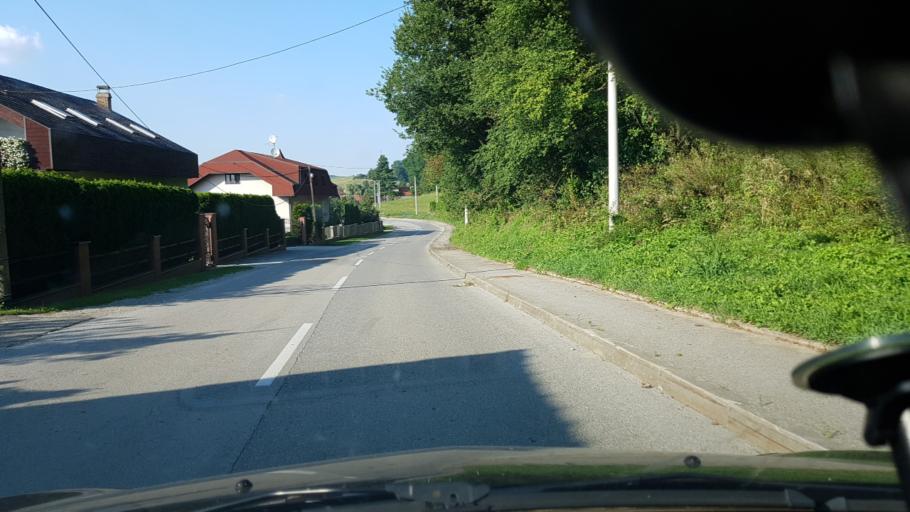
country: HR
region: Zagrebacka
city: Pojatno
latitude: 45.9451
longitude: 15.7300
